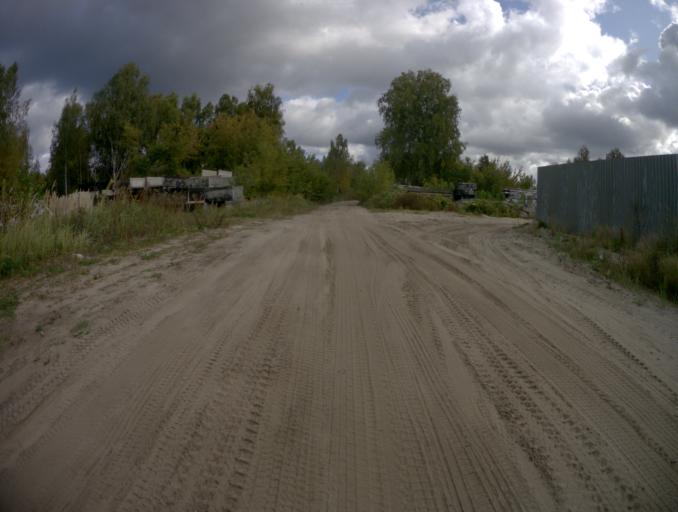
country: RU
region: Moskovskaya
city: Baksheyevo
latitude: 55.7113
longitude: 39.8867
